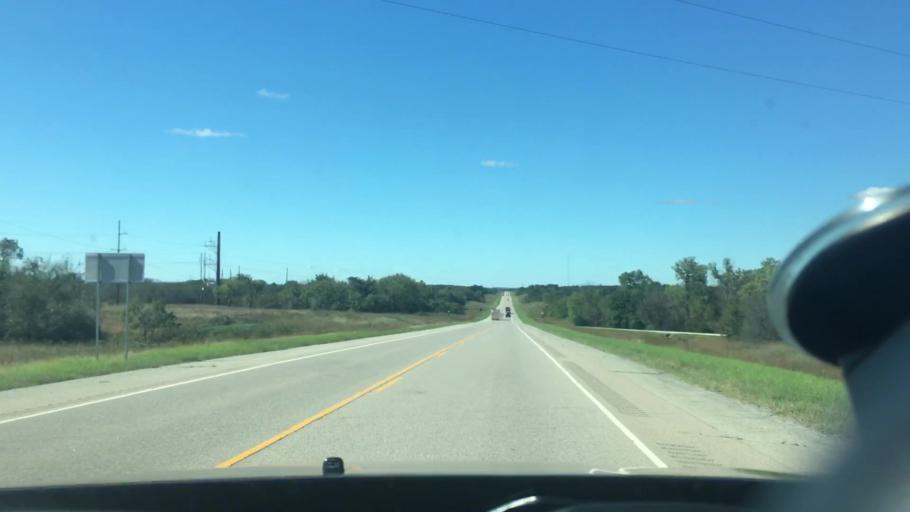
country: US
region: Oklahoma
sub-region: Coal County
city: Coalgate
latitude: 34.6202
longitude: -96.4526
